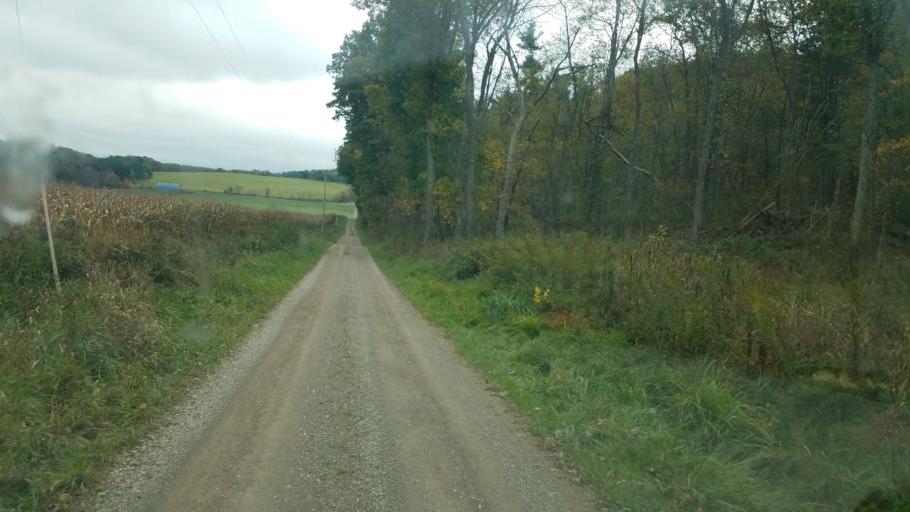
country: US
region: Ohio
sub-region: Ashland County
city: Loudonville
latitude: 40.6031
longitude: -82.1798
